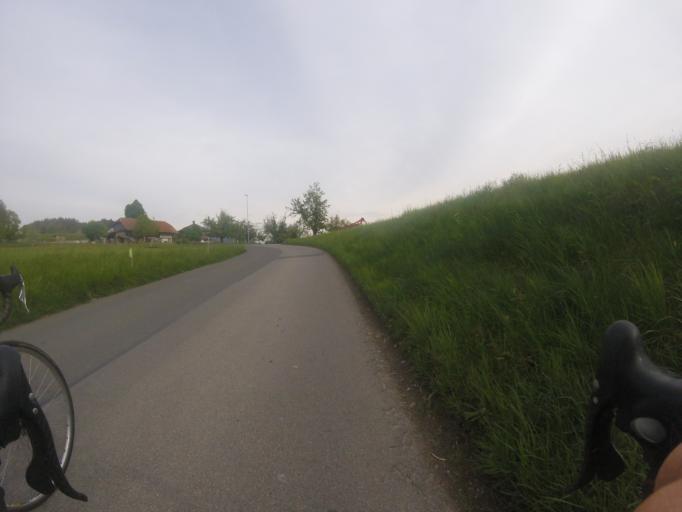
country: CH
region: Bern
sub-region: Bern-Mittelland District
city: Niederwichtrach
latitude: 46.8411
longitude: 7.5907
